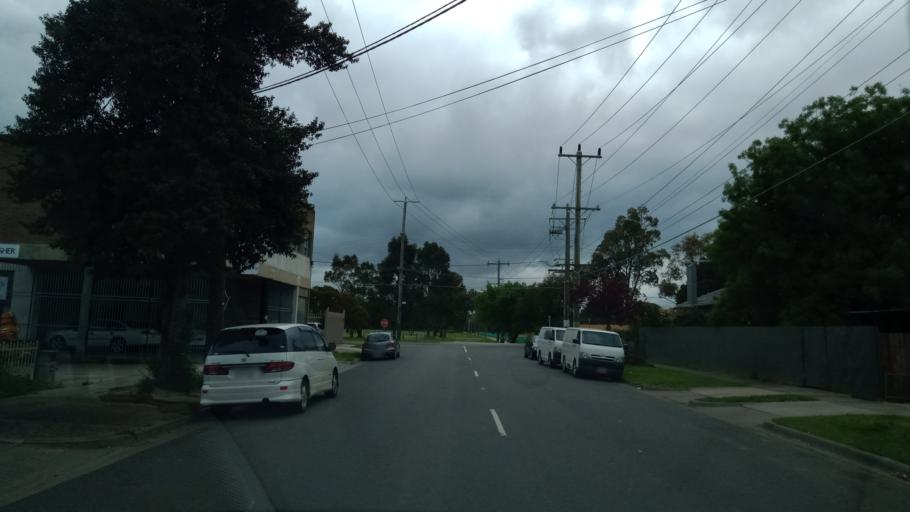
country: AU
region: Victoria
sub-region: Casey
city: Doveton
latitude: -37.9969
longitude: 145.2281
